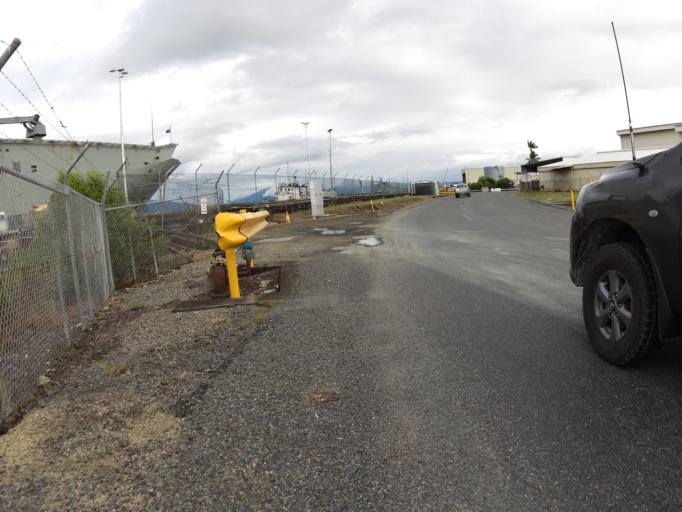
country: AU
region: Queensland
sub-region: Cairns
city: Cairns
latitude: -16.9311
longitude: 145.7792
